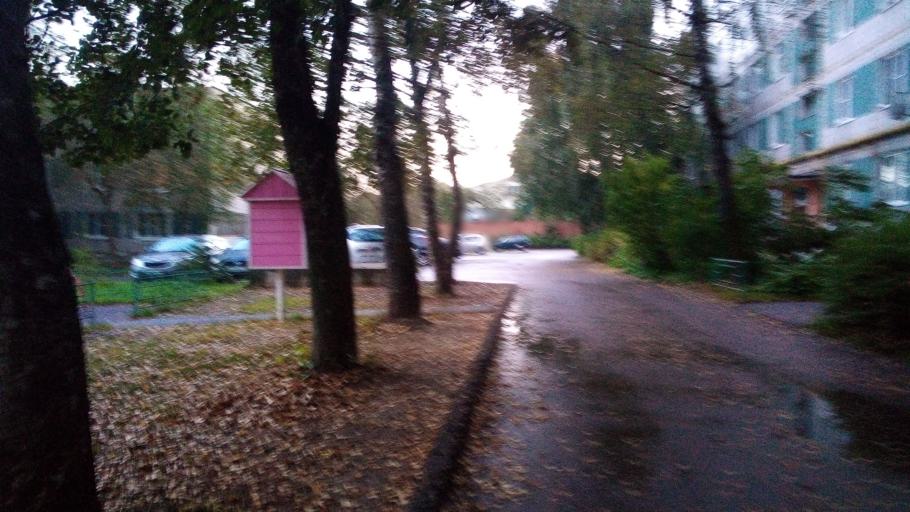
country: RU
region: Moskovskaya
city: Khot'kovo
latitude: 56.2463
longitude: 37.9422
